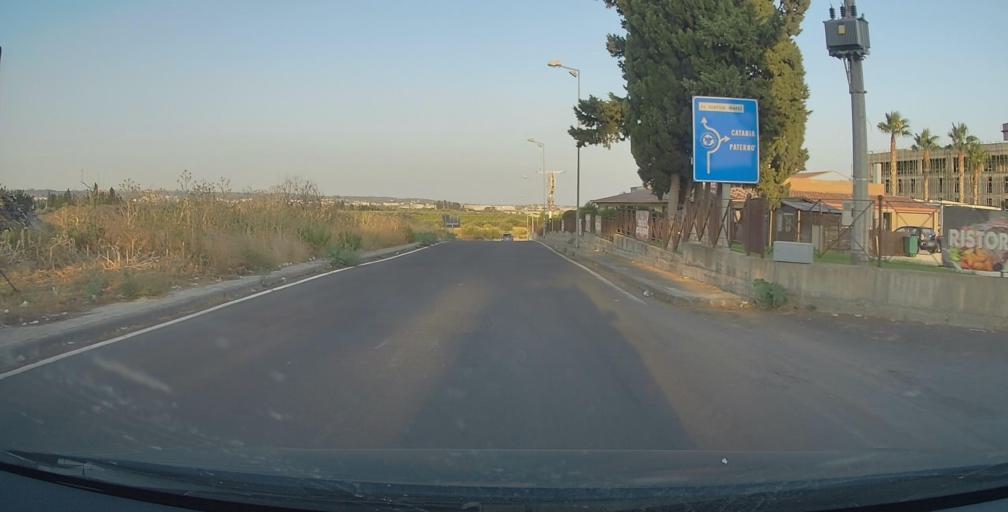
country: IT
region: Sicily
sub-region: Catania
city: Palazzolo
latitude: 37.5499
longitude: 14.9458
